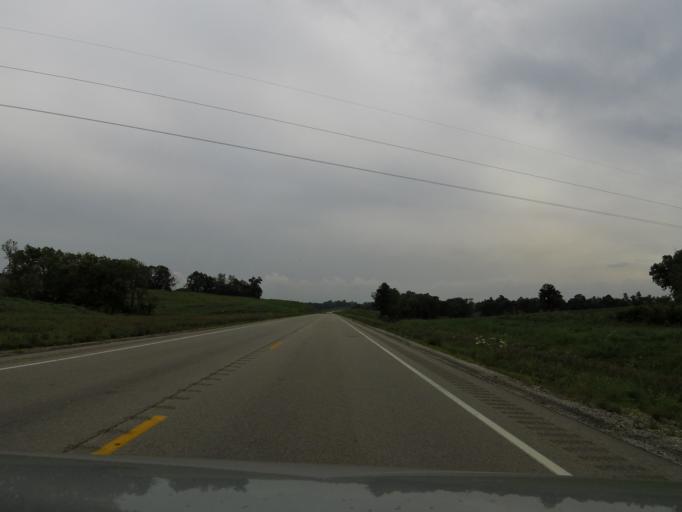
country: US
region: Ohio
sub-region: Brown County
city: Aberdeen
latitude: 38.6057
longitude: -83.8284
